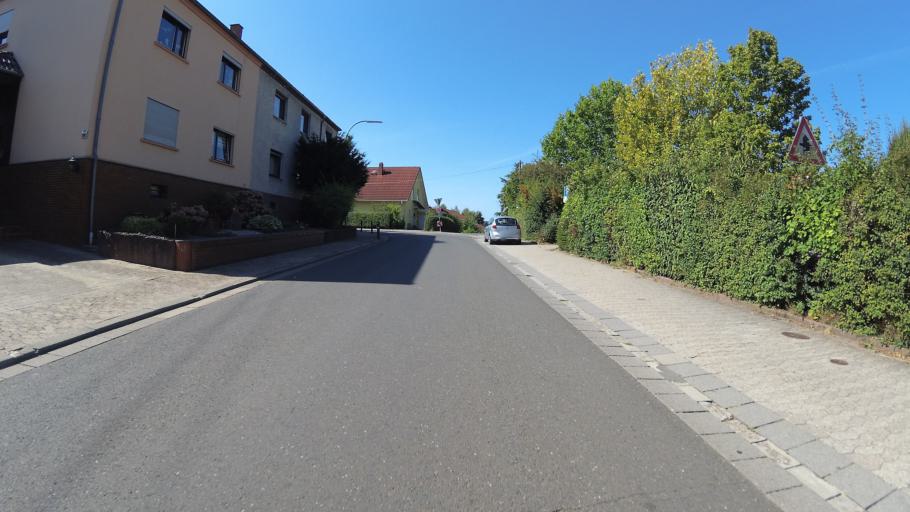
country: DE
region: Saarland
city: Illingen
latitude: 49.3767
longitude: 7.0456
